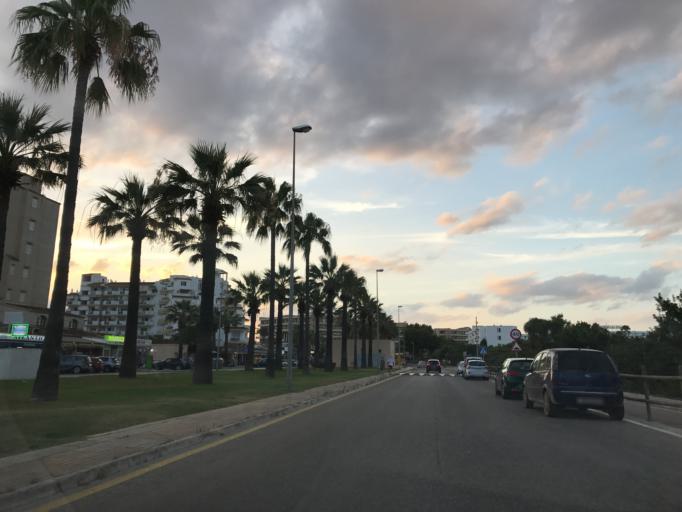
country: ES
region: Balearic Islands
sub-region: Illes Balears
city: Son Servera
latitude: 39.5771
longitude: 3.3774
